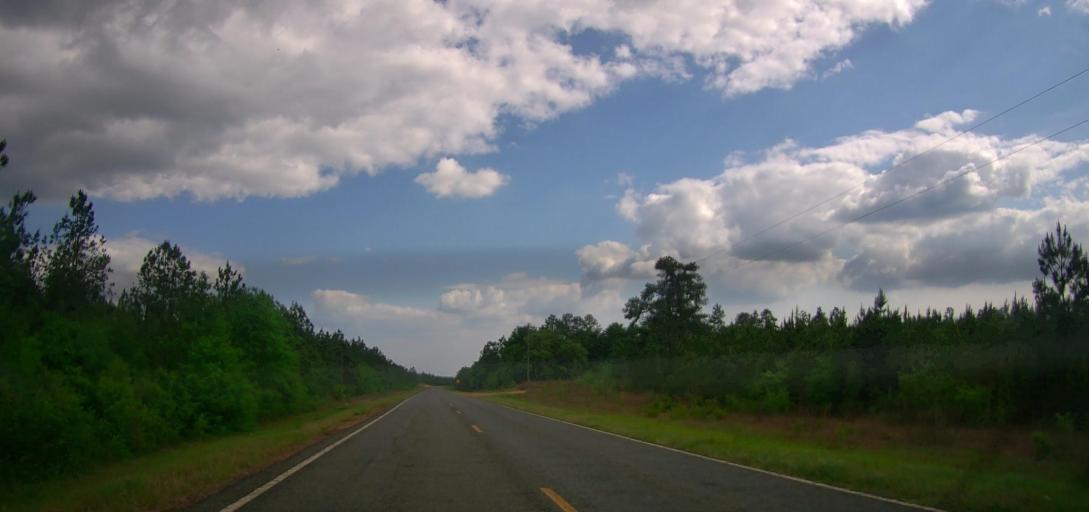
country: US
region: Georgia
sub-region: Johnson County
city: Wrightsville
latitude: 32.7575
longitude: -82.9286
